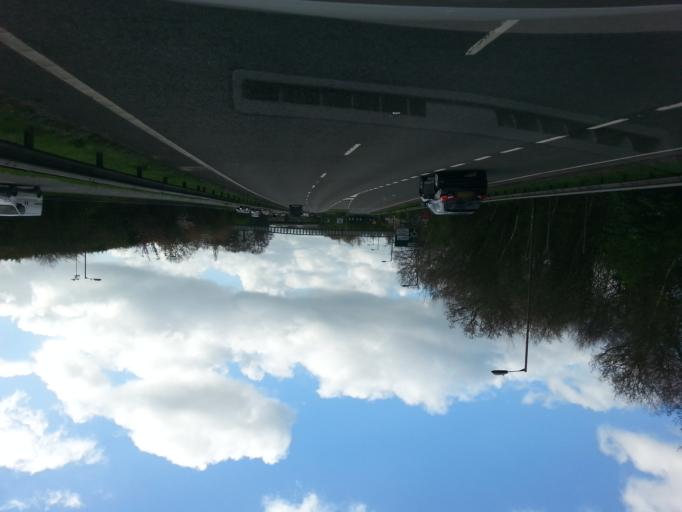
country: GB
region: England
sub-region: Hampshire
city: Farnborough
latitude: 51.2779
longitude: -0.7349
